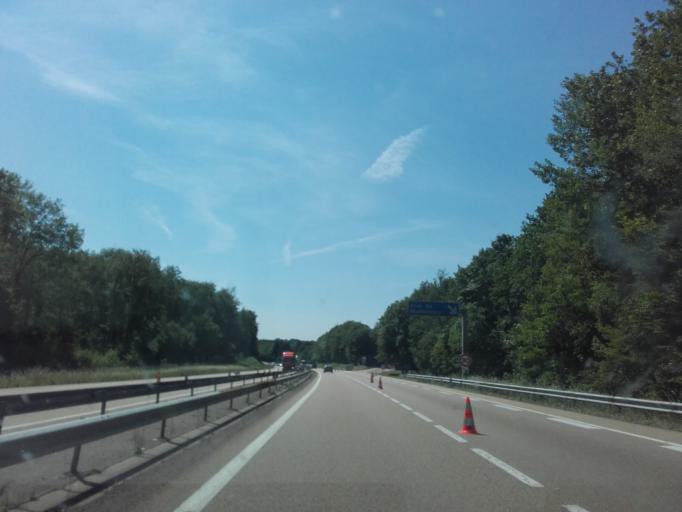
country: FR
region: Bourgogne
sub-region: Departement de l'Yonne
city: Joux-la-Ville
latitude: 47.6002
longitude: 3.9102
